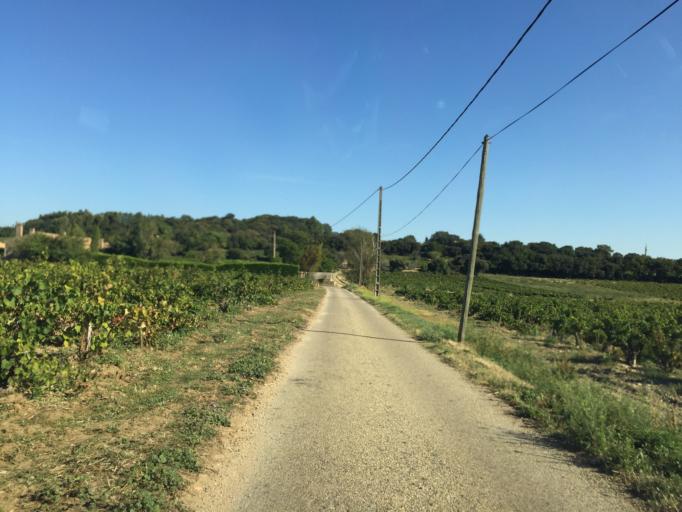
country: FR
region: Provence-Alpes-Cote d'Azur
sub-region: Departement du Vaucluse
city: Chateauneuf-du-Pape
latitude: 44.0578
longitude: 4.8378
